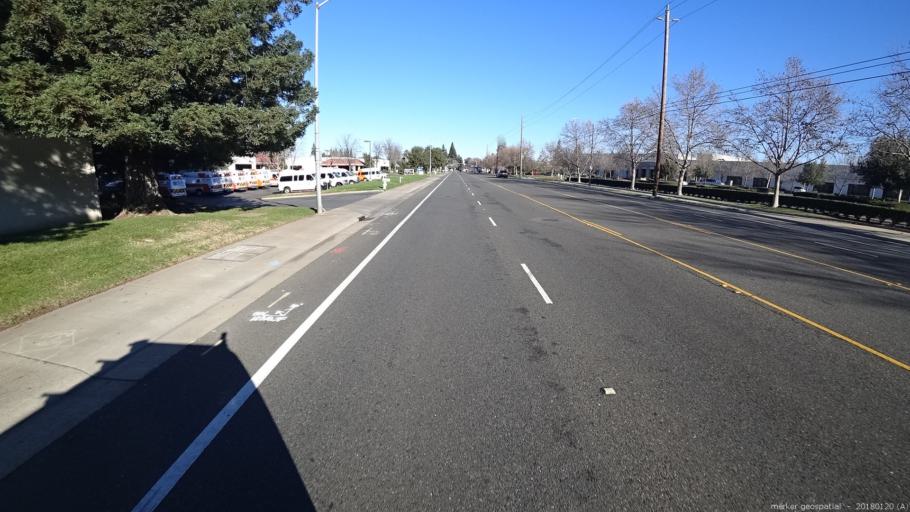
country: US
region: California
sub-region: Sacramento County
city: Rancho Cordova
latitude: 38.5713
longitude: -121.3069
